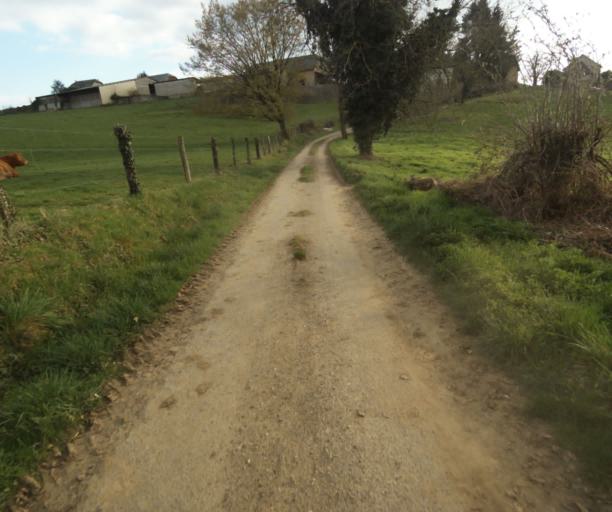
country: FR
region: Limousin
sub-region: Departement de la Correze
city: Saint-Clement
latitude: 45.3668
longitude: 1.6314
